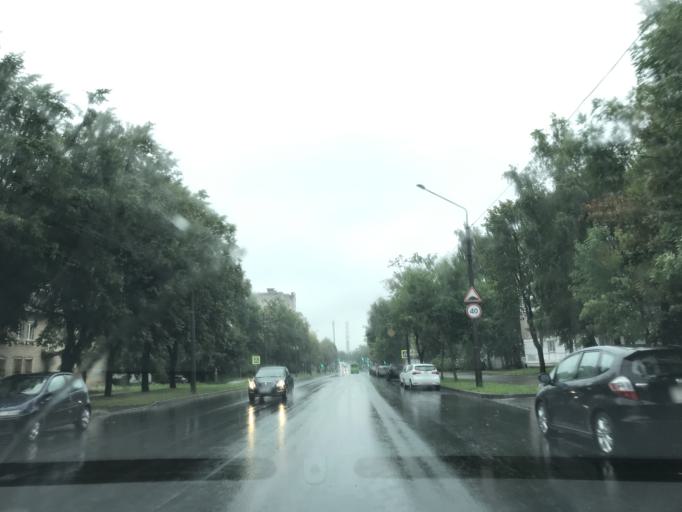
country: BY
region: Minsk
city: Minsk
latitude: 53.9375
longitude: 27.6105
